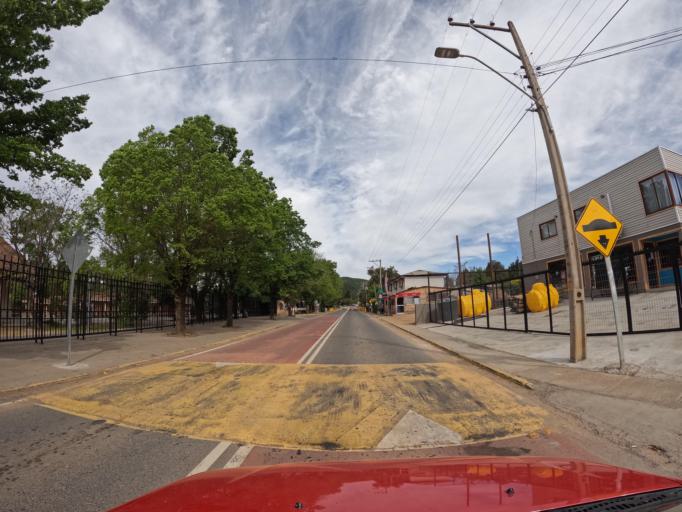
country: CL
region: Maule
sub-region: Provincia de Talca
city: Talca
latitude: -35.3208
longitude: -71.9571
